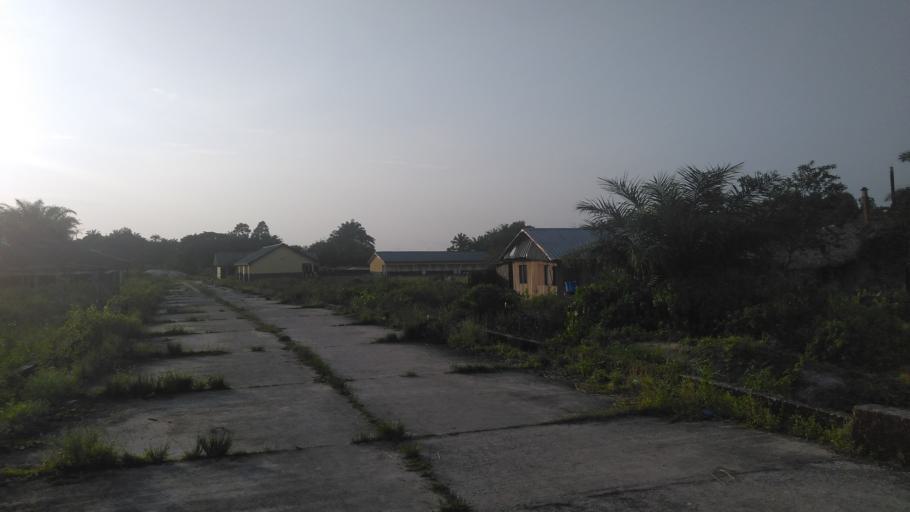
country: NG
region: Delta
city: Sapele
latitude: 5.8402
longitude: 5.1213
